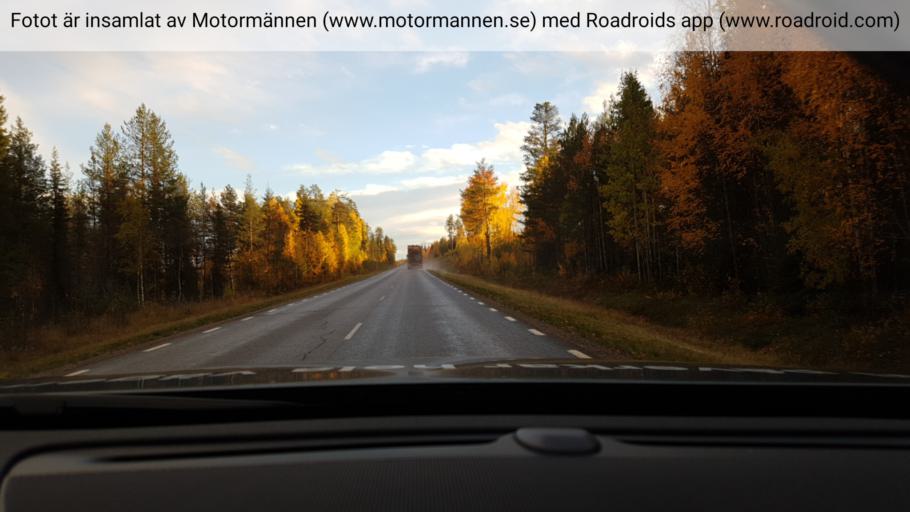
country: SE
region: Norrbotten
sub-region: Overkalix Kommun
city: OEverkalix
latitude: 66.6889
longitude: 22.6741
